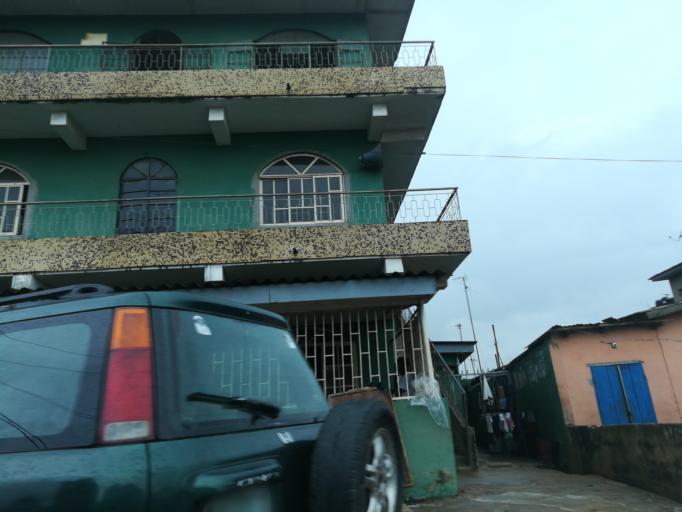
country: NG
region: Lagos
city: Oshodi
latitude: 6.5721
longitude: 3.3433
